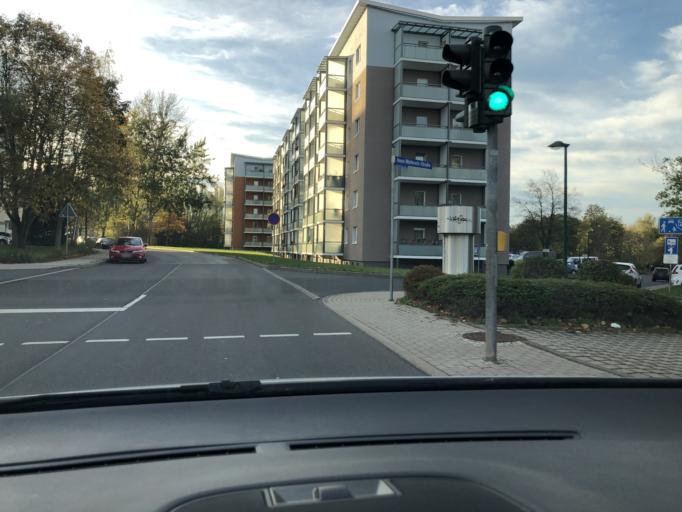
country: DE
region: Thuringia
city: Ilmenau
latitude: 50.6801
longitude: 10.9233
